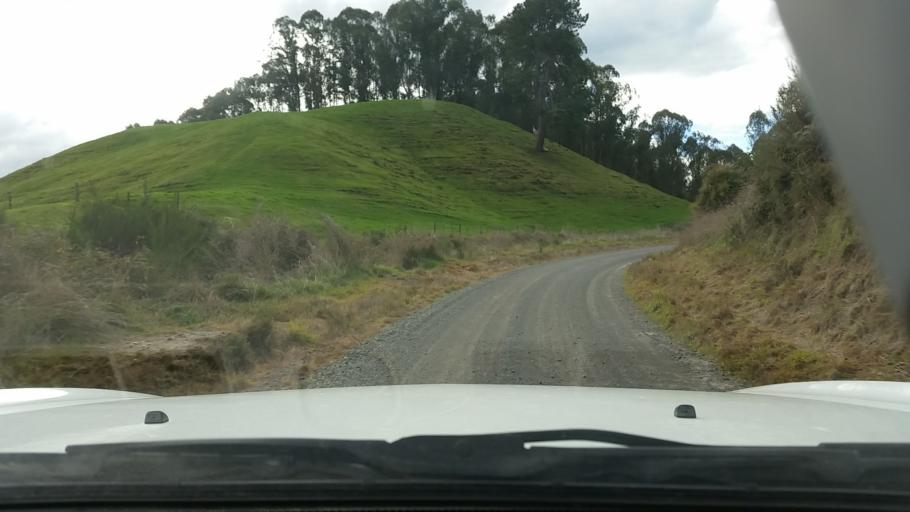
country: NZ
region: Waikato
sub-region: Taupo District
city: Taupo
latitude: -38.4927
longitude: 176.2066
